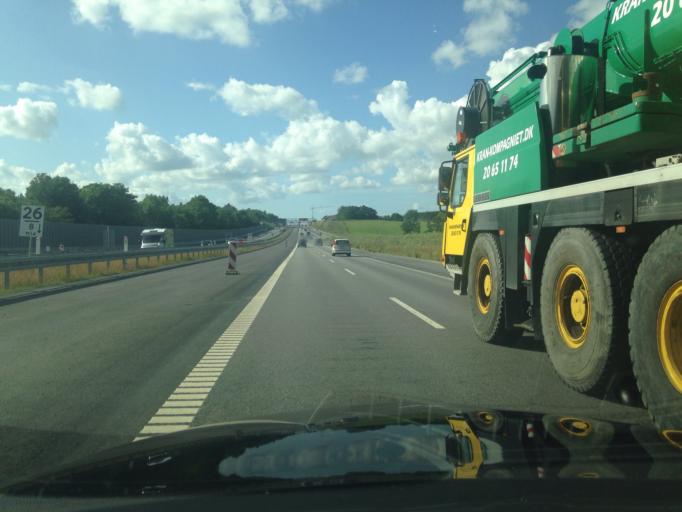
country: DK
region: Capital Region
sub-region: Rudersdal Kommune
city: Trorod
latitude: 55.8409
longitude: 12.5134
